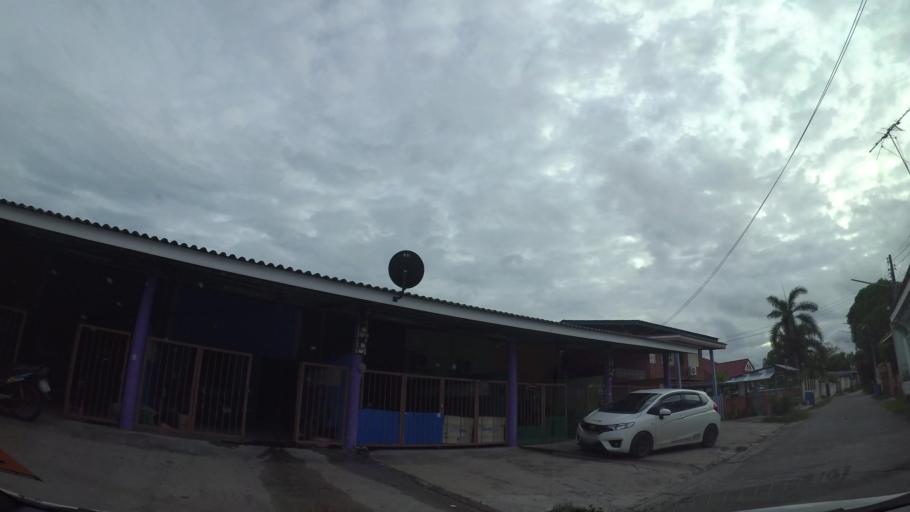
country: TH
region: Rayong
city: Rayong
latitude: 12.6765
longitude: 101.2642
